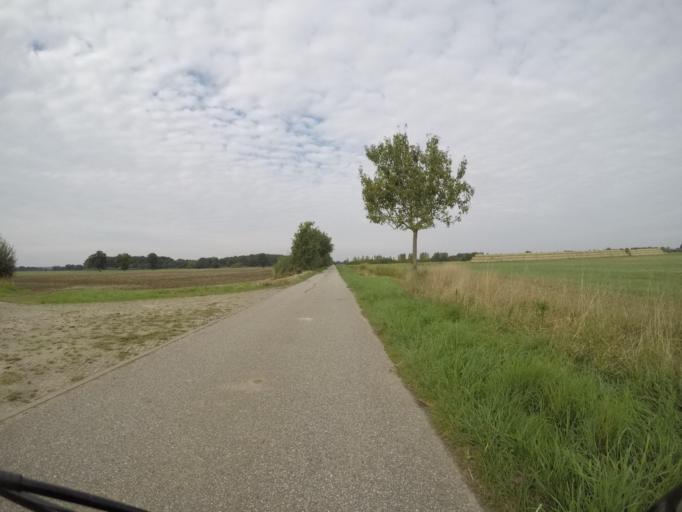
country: DE
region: Lower Saxony
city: Neu Darchau
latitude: 53.3010
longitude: 10.8802
